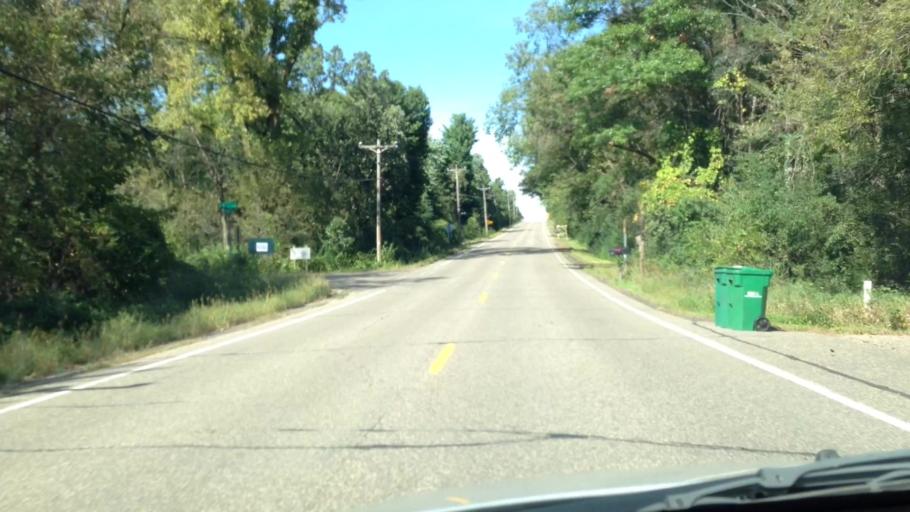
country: US
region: Minnesota
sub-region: Washington County
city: Stillwater
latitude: 45.0840
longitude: -92.8129
